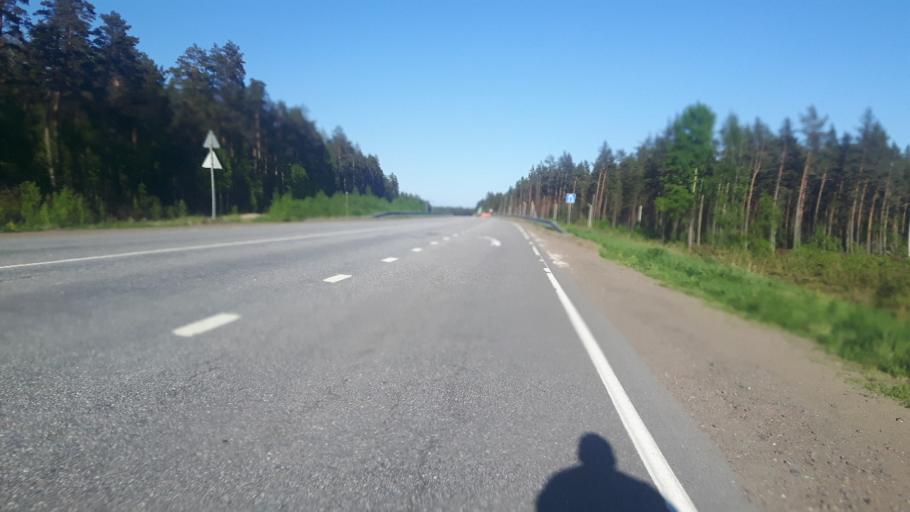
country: RU
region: Leningrad
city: Molodezhnoye
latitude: 60.1717
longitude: 29.3134
